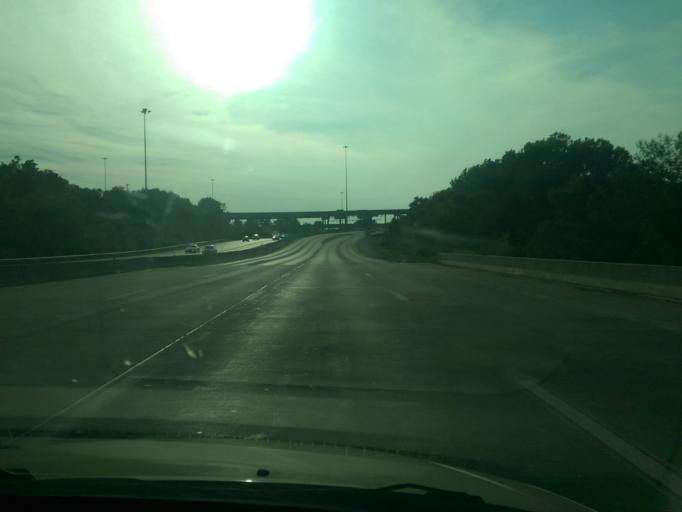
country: US
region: Missouri
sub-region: Platte County
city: Riverside
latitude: 39.1897
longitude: -94.6096
